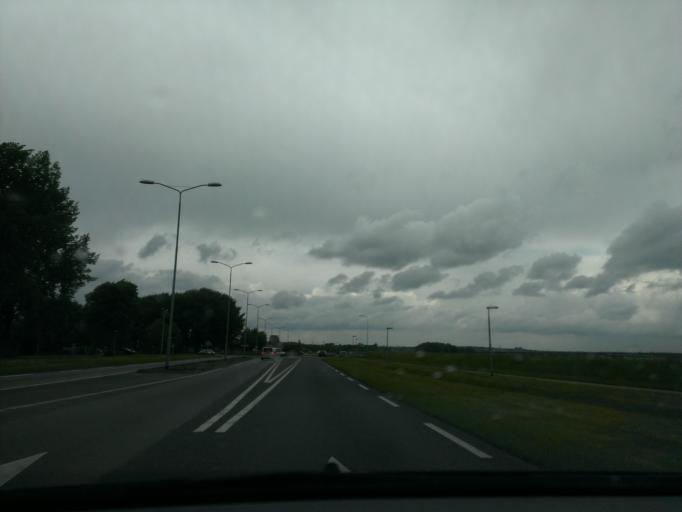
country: NL
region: Gelderland
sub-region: Gemeente Westervoort
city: Westervoort
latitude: 51.9475
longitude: 5.9351
